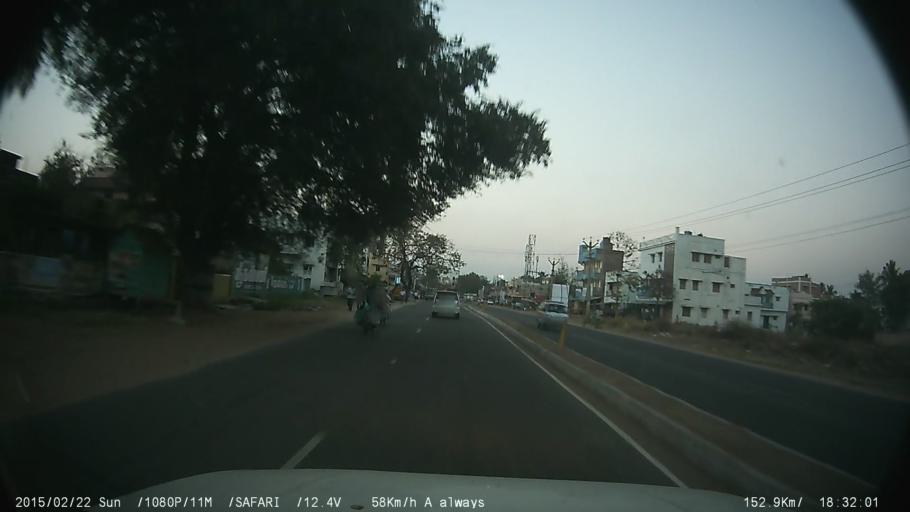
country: IN
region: Tamil Nadu
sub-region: Theni
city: Teni
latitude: 9.9980
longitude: 77.4658
